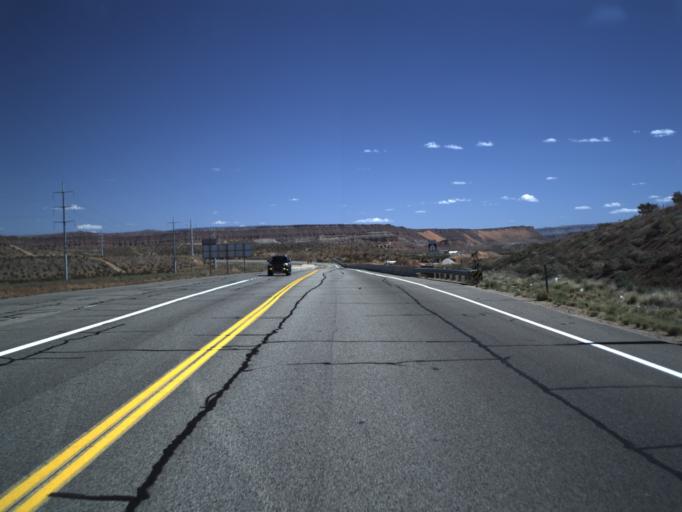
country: US
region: Utah
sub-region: Washington County
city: Washington
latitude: 37.0098
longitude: -113.5072
